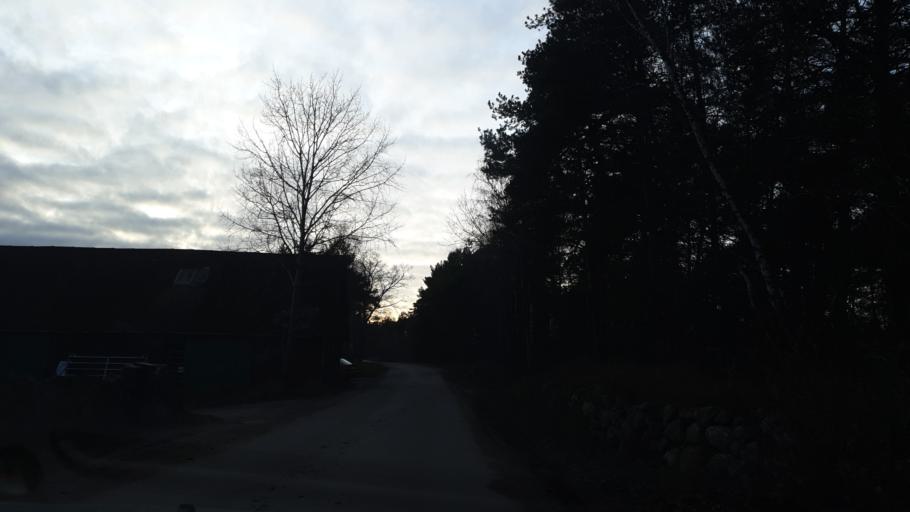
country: SE
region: Blekinge
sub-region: Karlskrona Kommun
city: Jaemjoe
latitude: 56.1577
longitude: 15.9100
